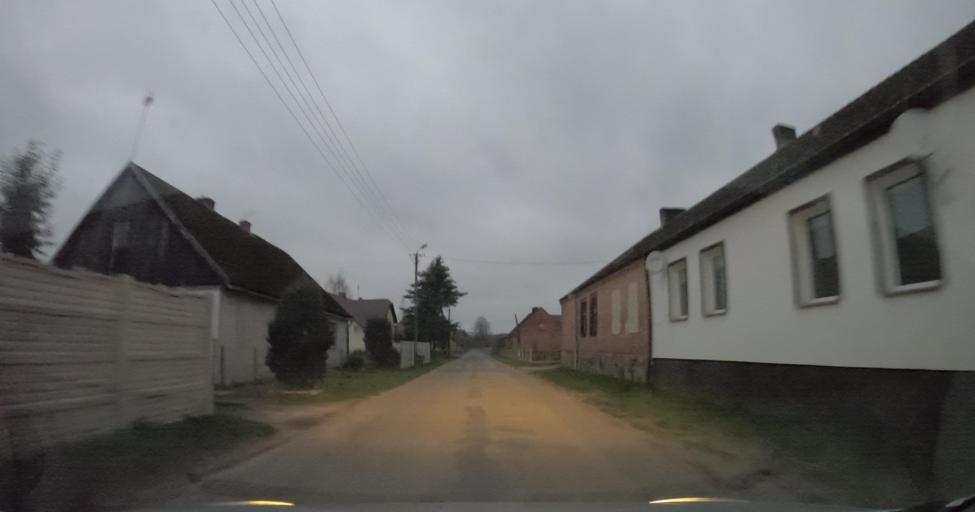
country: PL
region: West Pomeranian Voivodeship
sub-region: Powiat bialogardzki
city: Tychowo
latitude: 53.8574
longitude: 16.2433
